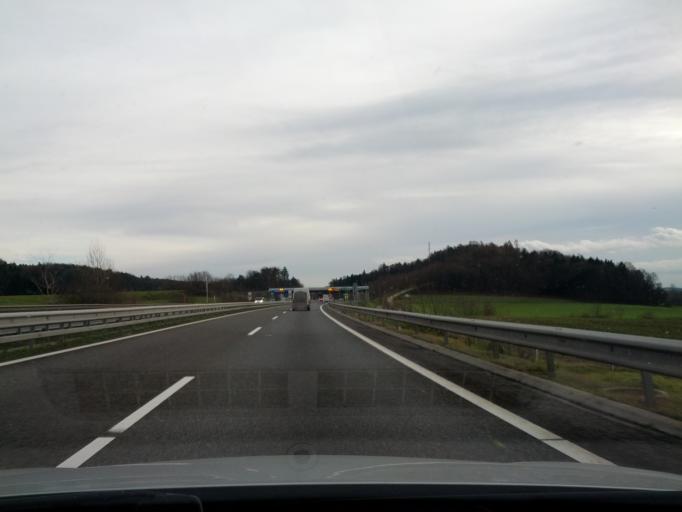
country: SI
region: Sveti Jurij
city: Sveti Jurij ob Scavnici
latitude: 46.5840
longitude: 16.0380
